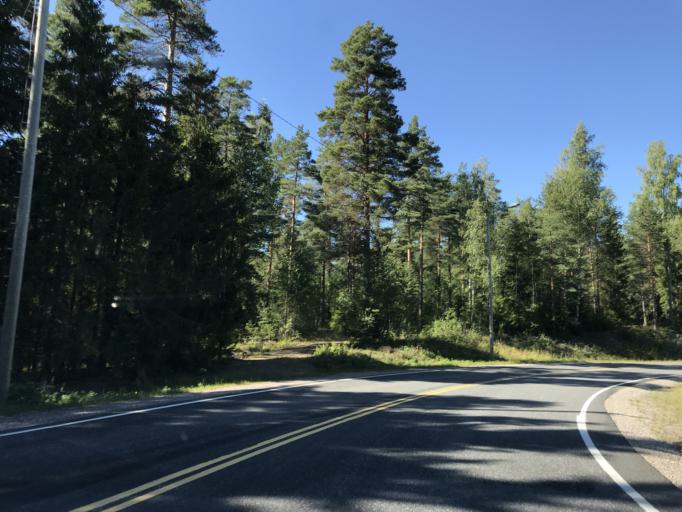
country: FI
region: Uusimaa
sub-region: Helsinki
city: Nurmijaervi
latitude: 60.5087
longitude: 24.6283
